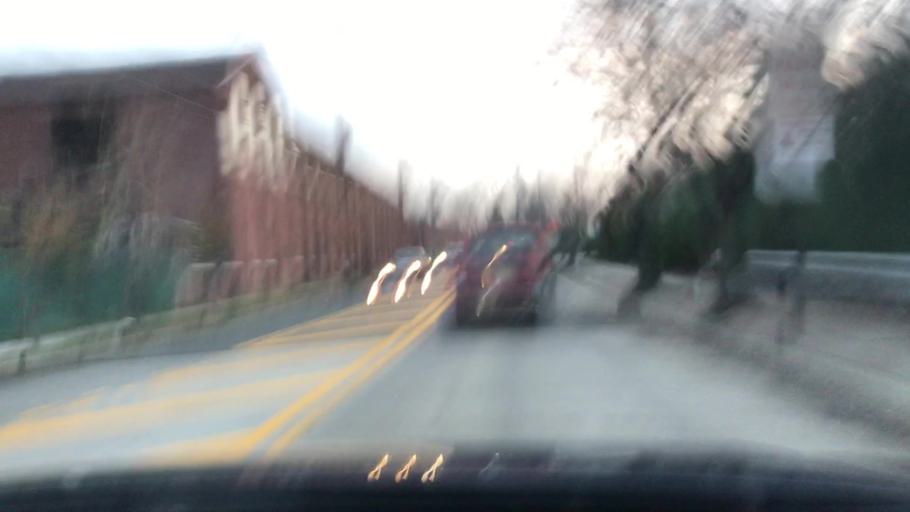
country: US
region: New Jersey
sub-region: Bergen County
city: Wallington
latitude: 40.8631
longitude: -74.1060
